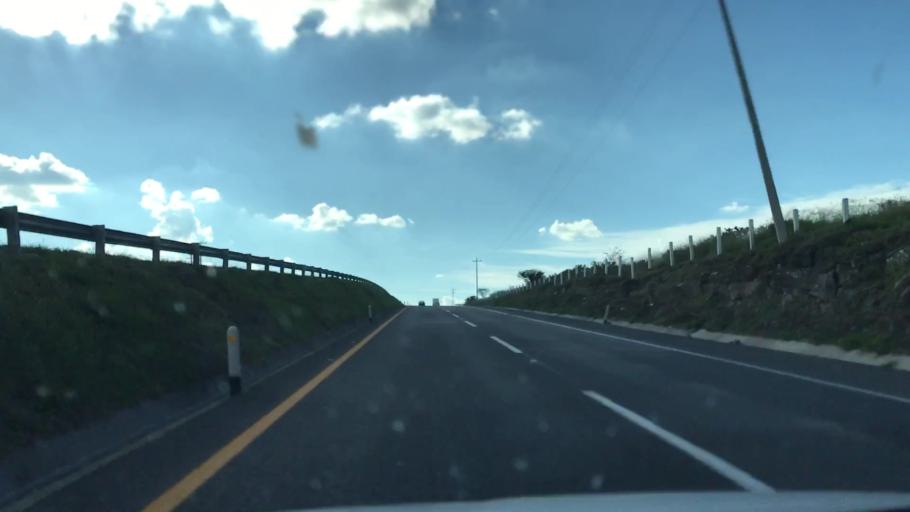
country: MX
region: Jalisco
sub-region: San Juan de los Lagos
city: Mezquitic de la Magdalena
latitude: 21.2896
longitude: -102.1943
